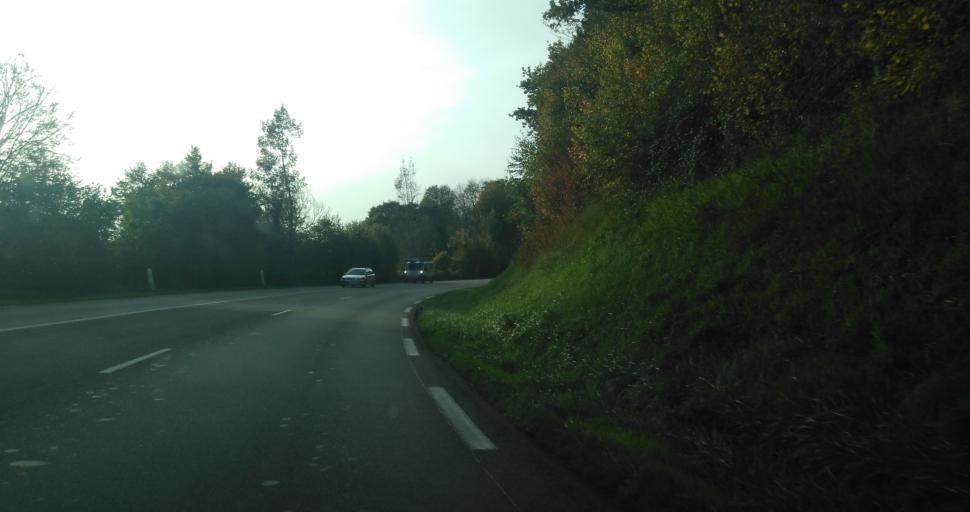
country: FR
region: Haute-Normandie
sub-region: Departement de l'Eure
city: Toutainville
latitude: 49.3600
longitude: 0.4551
